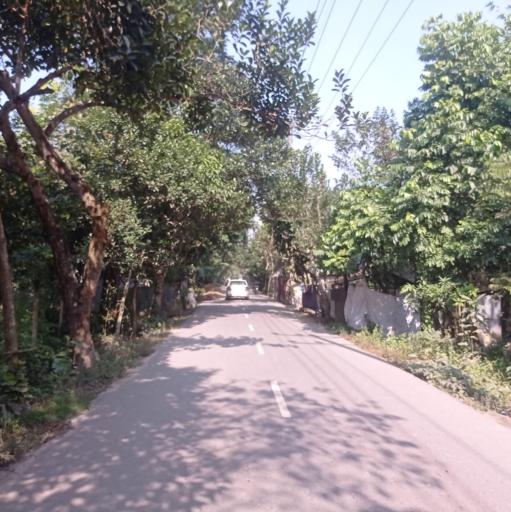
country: BD
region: Dhaka
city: Narsingdi
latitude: 24.0707
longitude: 90.6925
